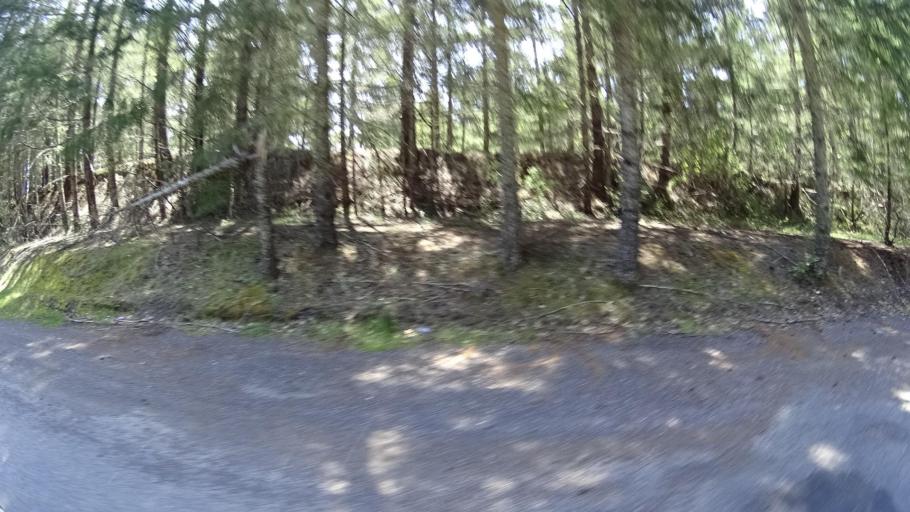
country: US
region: California
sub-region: Humboldt County
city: Redway
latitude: 40.1204
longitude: -123.6689
